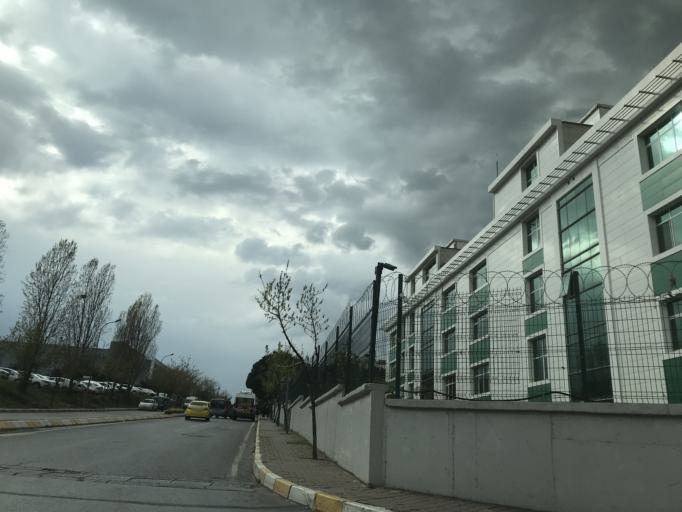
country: TR
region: Istanbul
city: Samandira
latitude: 40.9957
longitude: 29.1774
